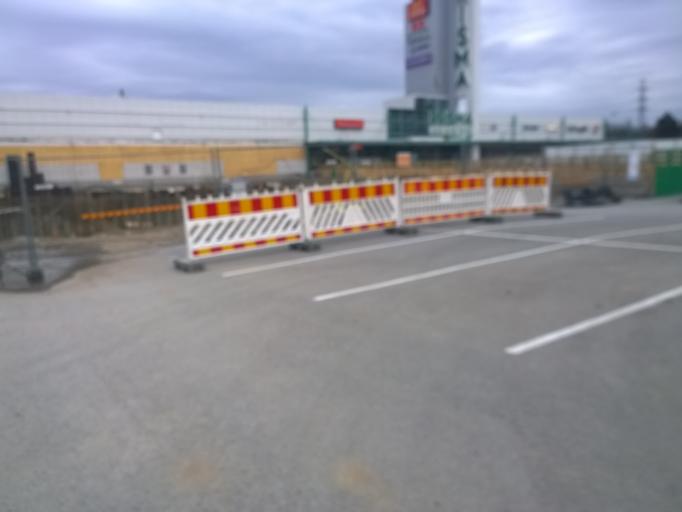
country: FI
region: Pirkanmaa
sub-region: Tampere
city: Tampere
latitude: 61.4909
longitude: 23.8198
